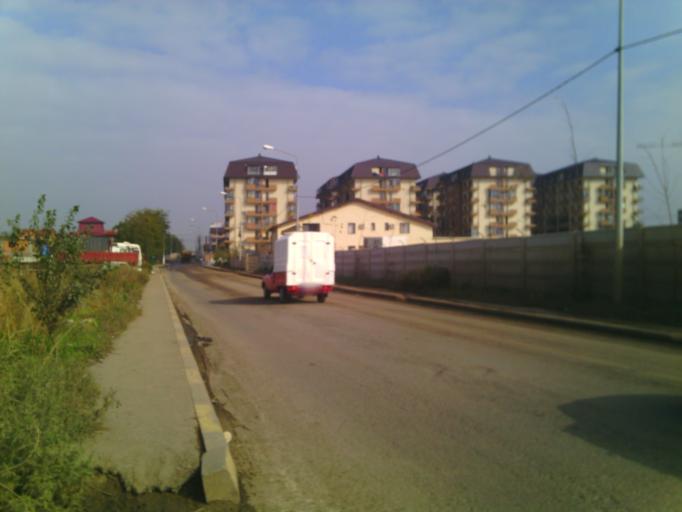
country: RO
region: Ilfov
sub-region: Comuna Magurele
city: Magurele
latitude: 44.3866
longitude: 26.0590
